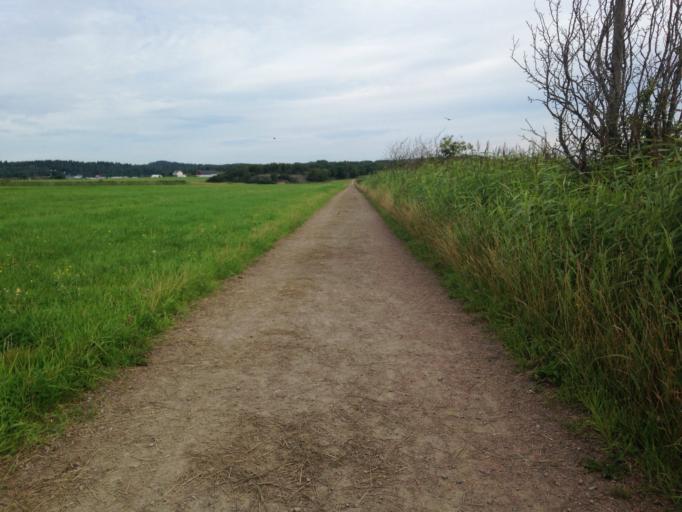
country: SE
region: Vaestra Goetaland
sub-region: Kungalvs Kommun
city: Kungalv
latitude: 57.8044
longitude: 11.8852
